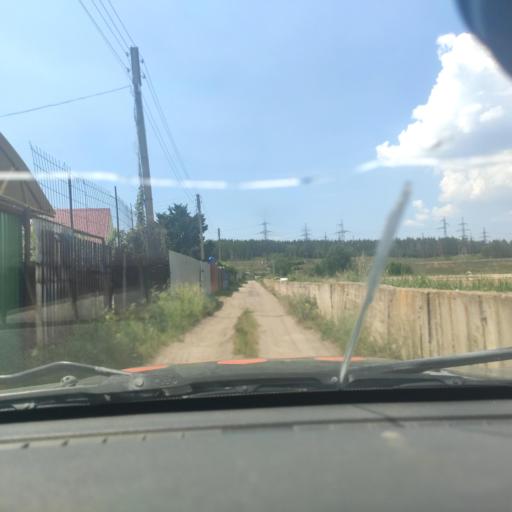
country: RU
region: Samara
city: Zhigulevsk
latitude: 53.5006
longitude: 49.4972
